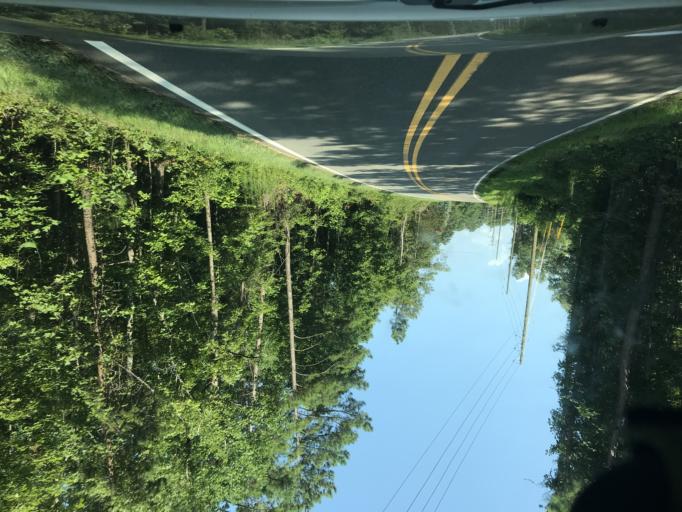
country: US
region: Georgia
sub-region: Hall County
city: Flowery Branch
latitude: 34.2319
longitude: -84.0028
